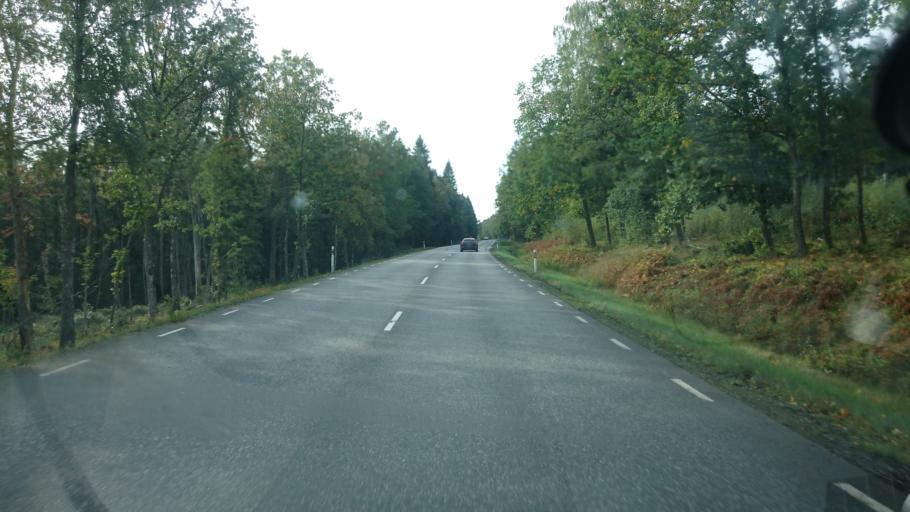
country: SE
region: Vaestra Goetaland
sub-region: Alingsas Kommun
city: Sollebrunn
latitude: 58.0240
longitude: 12.4594
